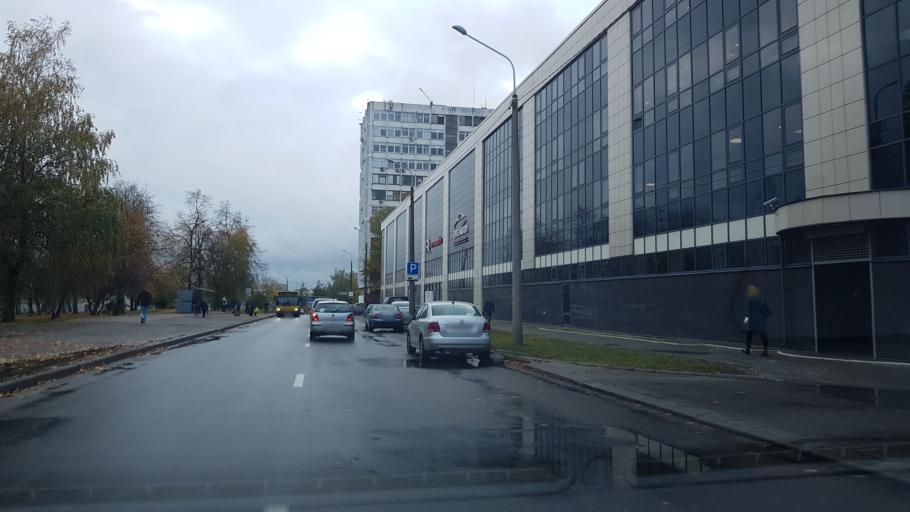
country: BY
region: Minsk
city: Minsk
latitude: 53.8926
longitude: 27.5881
